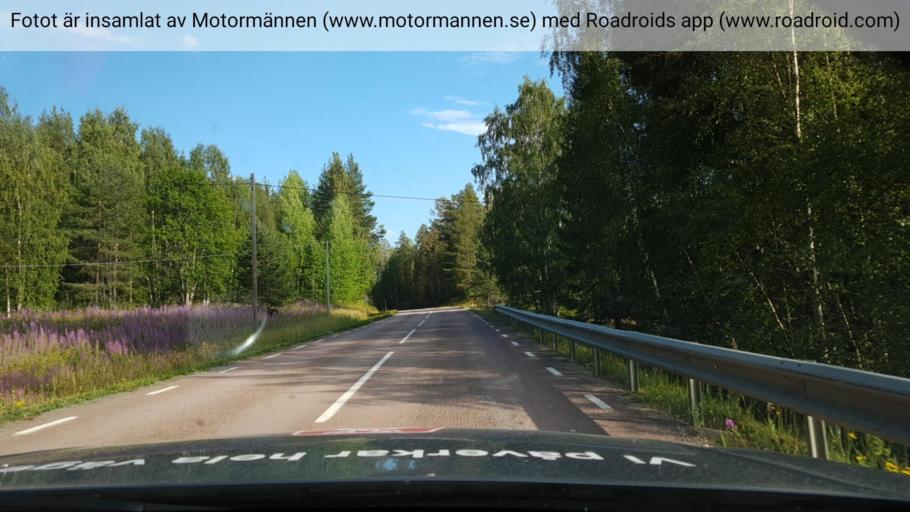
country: SE
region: Vaesternorrland
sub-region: Solleftea Kommun
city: As
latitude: 63.5983
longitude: 16.2264
